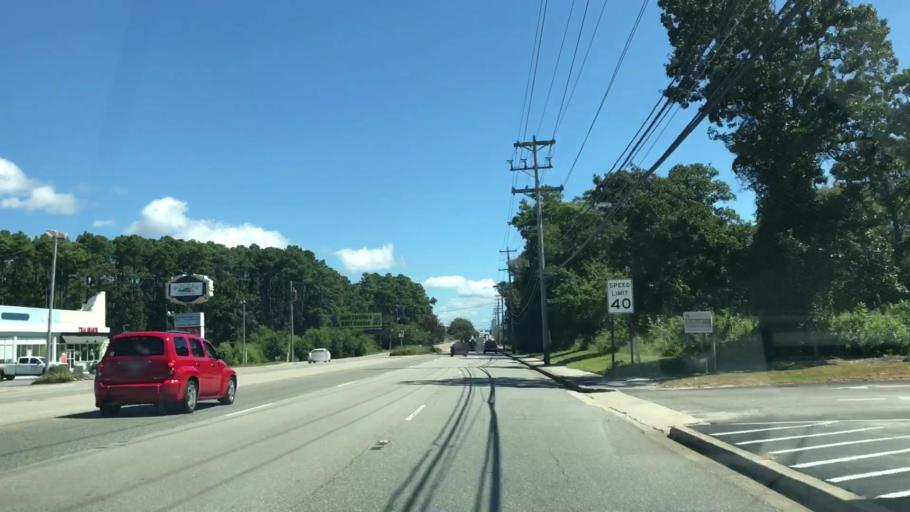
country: US
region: South Carolina
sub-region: Horry County
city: North Myrtle Beach
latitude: 33.8186
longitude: -78.6917
